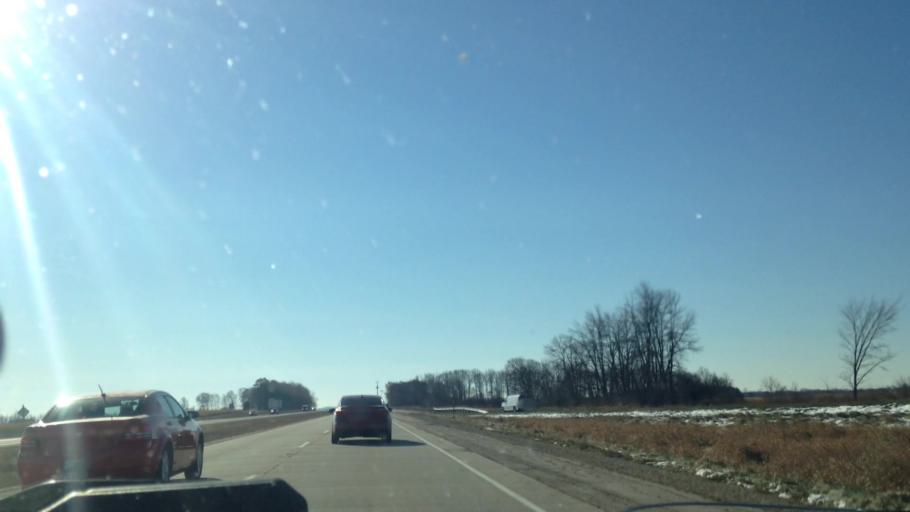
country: US
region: Wisconsin
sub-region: Washington County
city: Jackson
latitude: 43.3518
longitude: -88.1908
